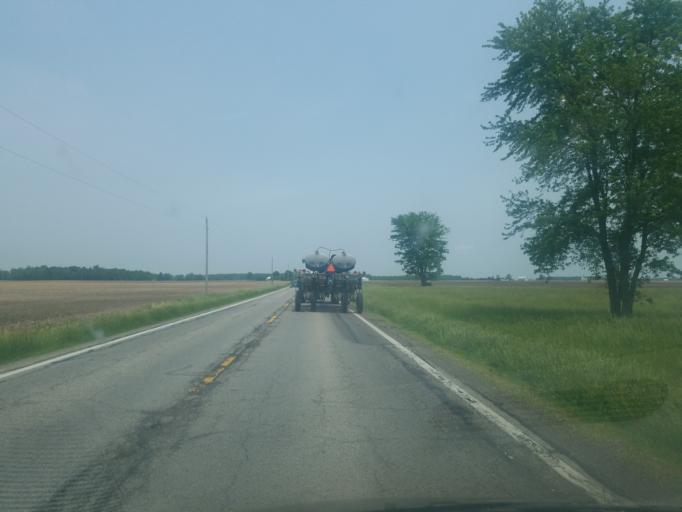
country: US
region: Ohio
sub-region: Marion County
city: Marion
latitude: 40.6964
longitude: -83.0812
